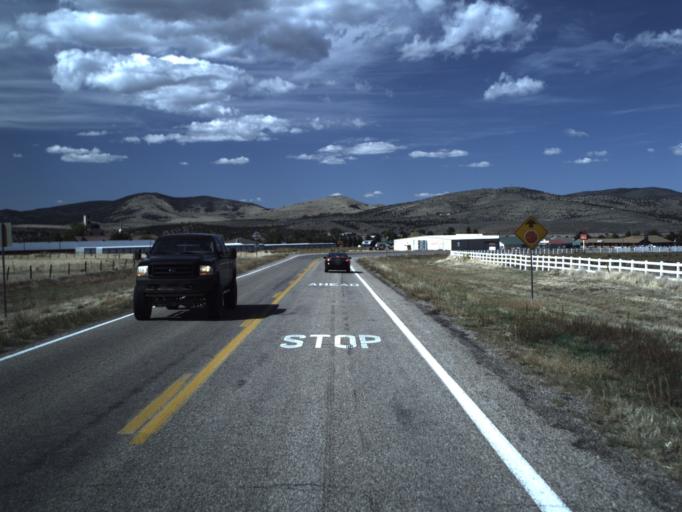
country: US
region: Utah
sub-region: Washington County
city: Enterprise
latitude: 37.5711
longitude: -113.7024
